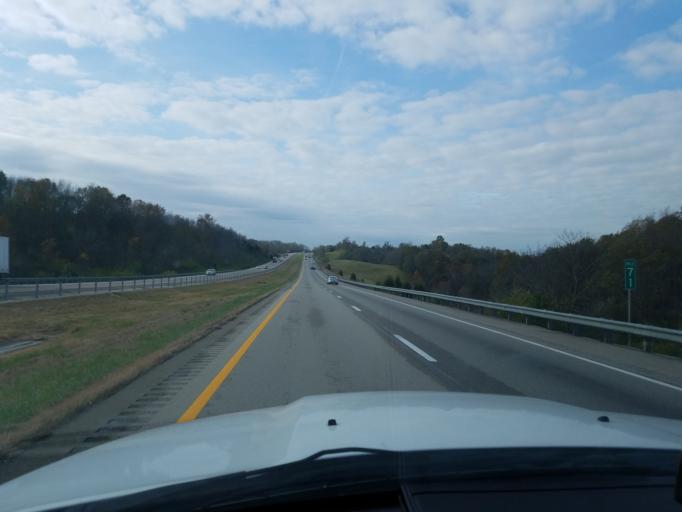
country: US
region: Kentucky
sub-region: Boone County
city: Verona
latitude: 38.8234
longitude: -84.6980
